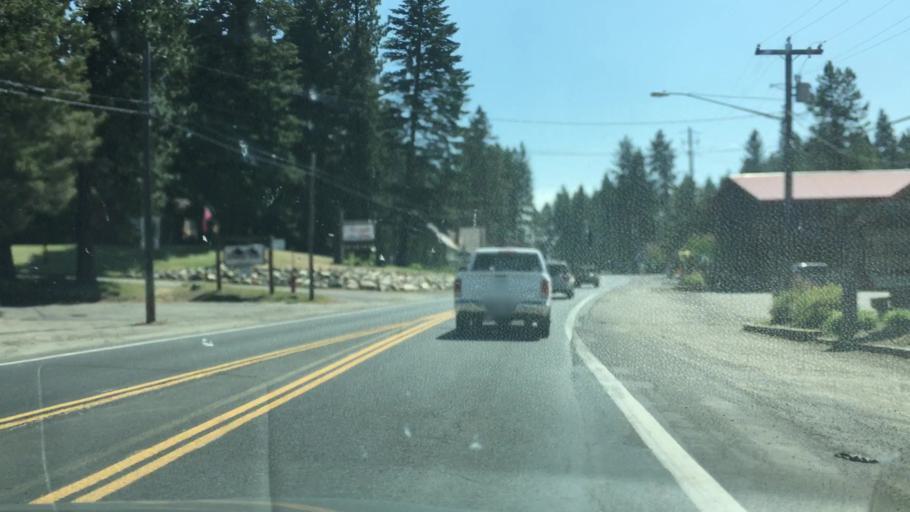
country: US
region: Idaho
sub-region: Valley County
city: McCall
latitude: 44.9053
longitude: -116.0977
